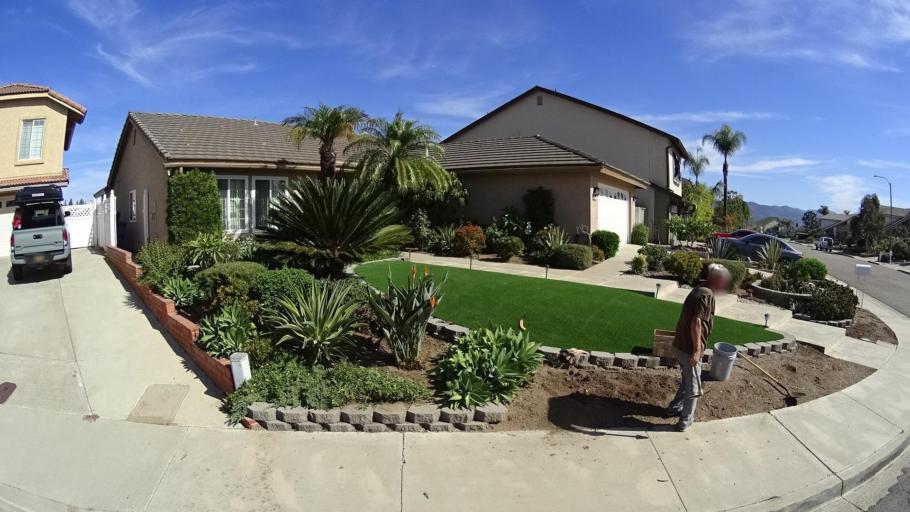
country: US
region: California
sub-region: San Diego County
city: Rancho San Diego
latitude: 32.7494
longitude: -116.9531
